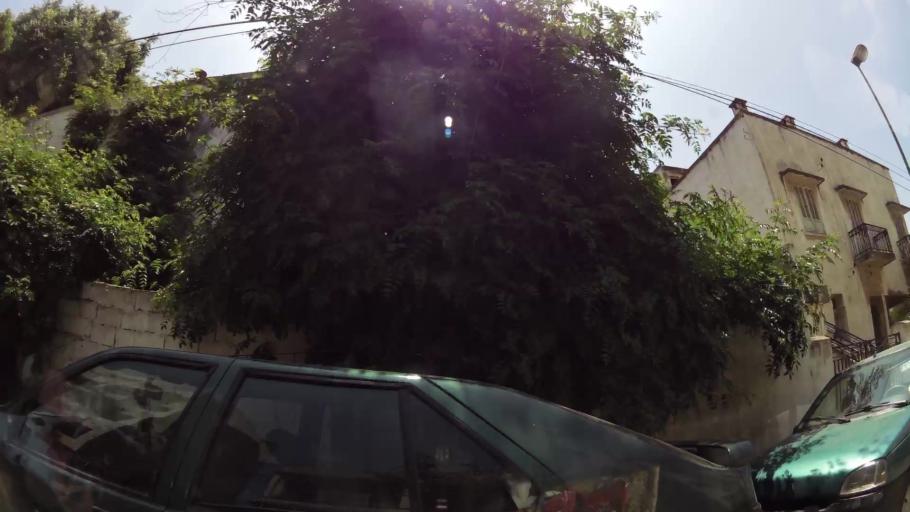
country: MA
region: Rabat-Sale-Zemmour-Zaer
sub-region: Rabat
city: Rabat
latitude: 34.0121
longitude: -6.8273
